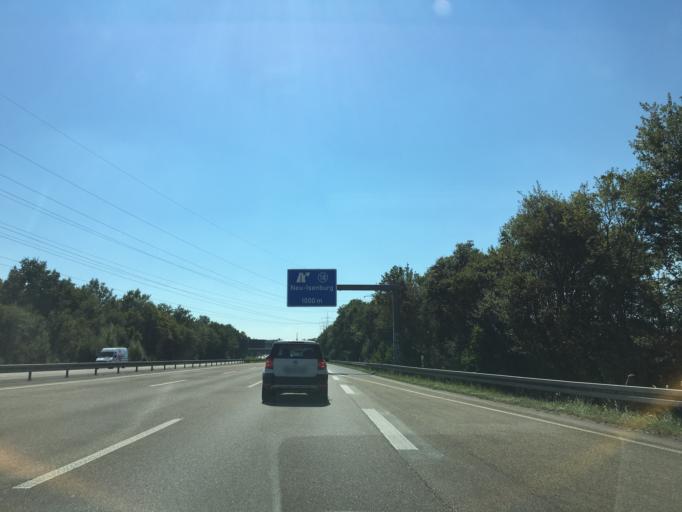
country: DE
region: Hesse
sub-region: Regierungsbezirk Darmstadt
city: Neu Isenburg
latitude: 50.0588
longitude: 8.7245
